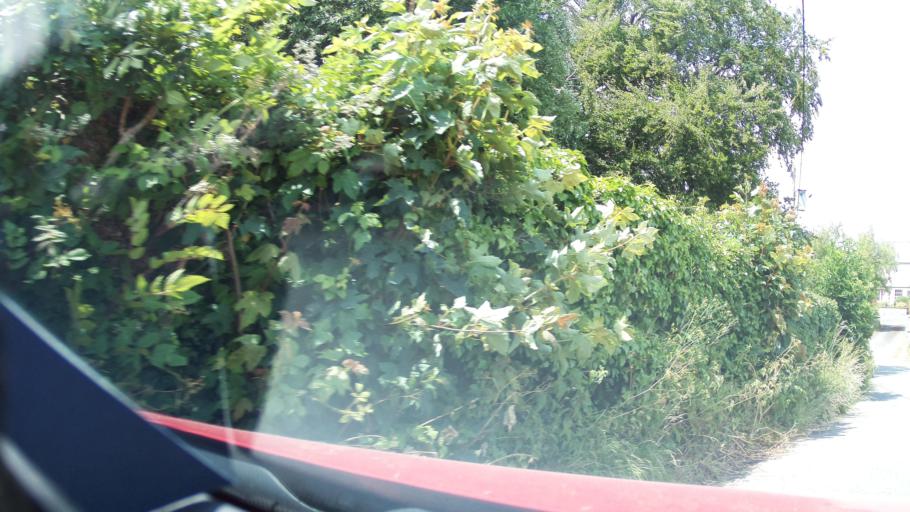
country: GB
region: Wales
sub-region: Vale of Glamorgan
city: Wick
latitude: 51.4053
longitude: -3.5297
